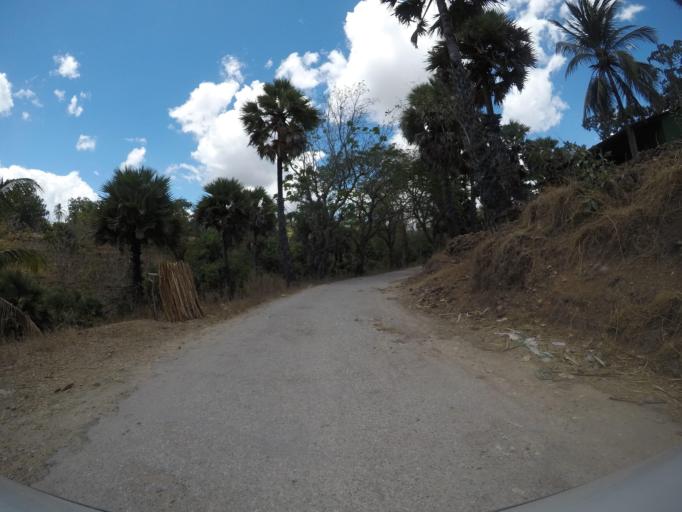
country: TL
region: Baucau
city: Baucau
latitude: -8.4836
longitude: 126.6350
